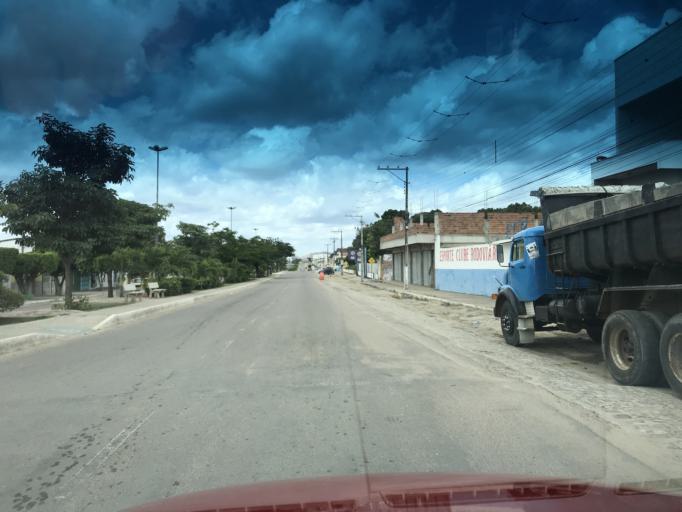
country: BR
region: Bahia
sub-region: Itaberaba
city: Itaberaba
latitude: -12.5195
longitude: -40.3058
